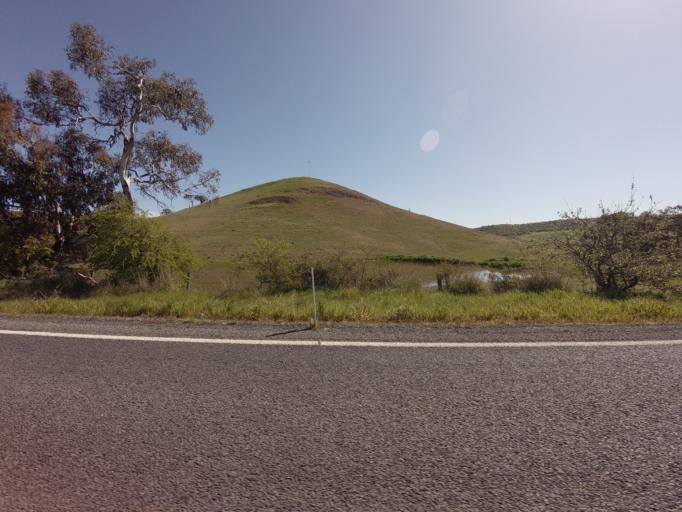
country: AU
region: Tasmania
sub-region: Derwent Valley
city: New Norfolk
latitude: -42.5732
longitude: 146.8821
